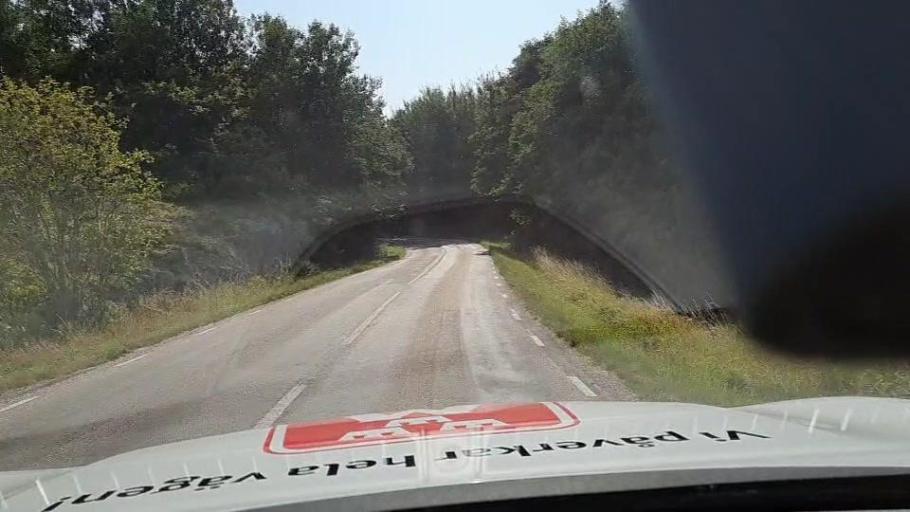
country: SE
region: Vaestra Goetaland
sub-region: Tjorns Kommun
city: Skaerhamn
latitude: 58.0953
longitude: 11.4909
